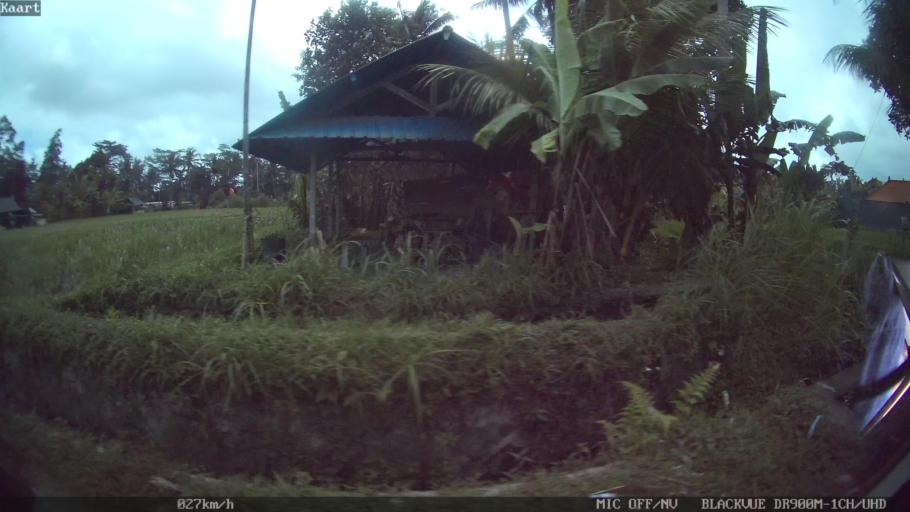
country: ID
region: Bali
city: Banjar Petak
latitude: -8.4411
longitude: 115.3229
